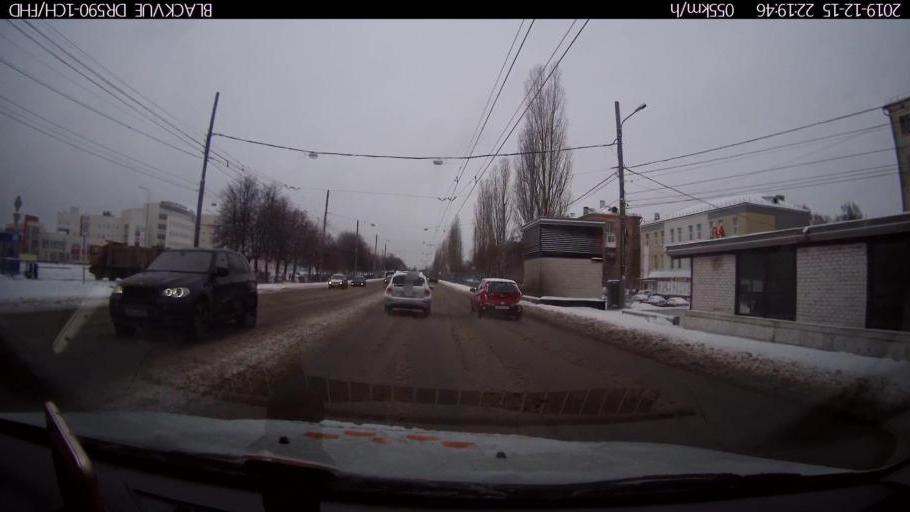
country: RU
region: Nizjnij Novgorod
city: Nizhniy Novgorod
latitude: 56.3264
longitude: 43.9107
